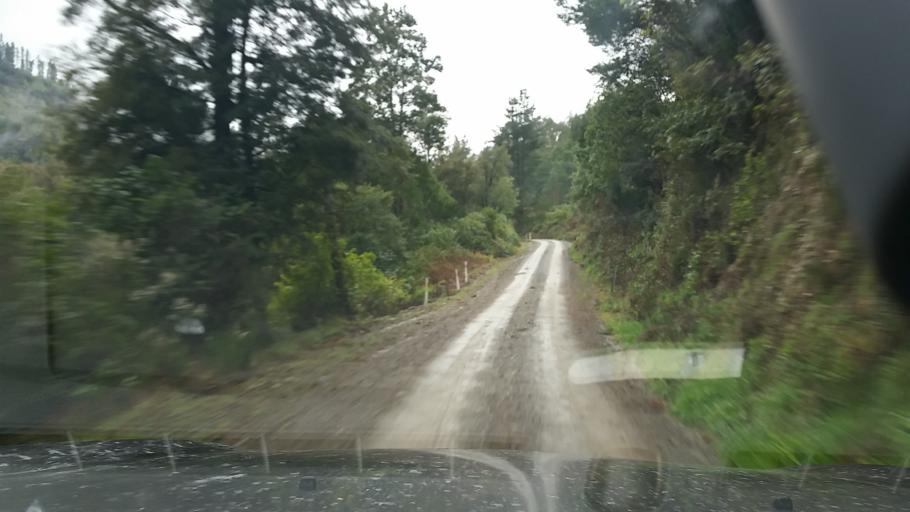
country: NZ
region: Nelson
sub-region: Nelson City
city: Nelson
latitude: -41.3597
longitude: 173.6185
